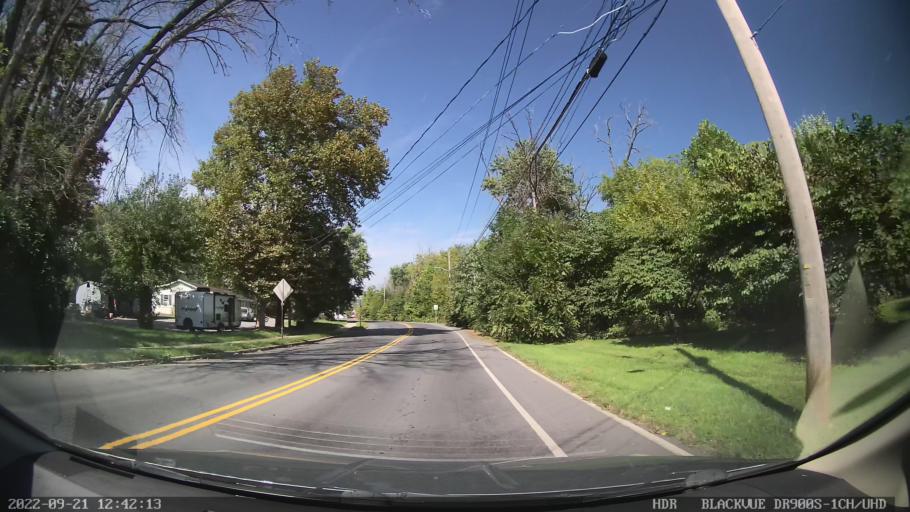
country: US
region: Pennsylvania
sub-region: Berks County
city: Kutztown
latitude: 40.5155
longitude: -75.7725
